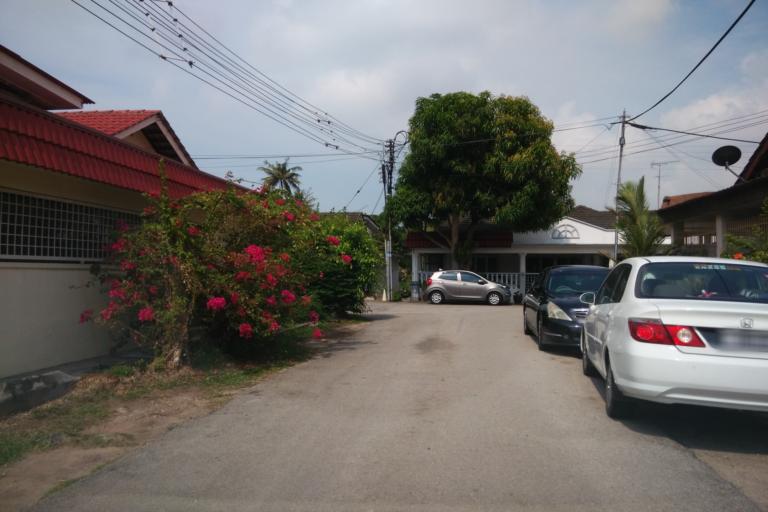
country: MY
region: Melaka
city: Malacca
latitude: 2.2095
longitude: 102.2421
